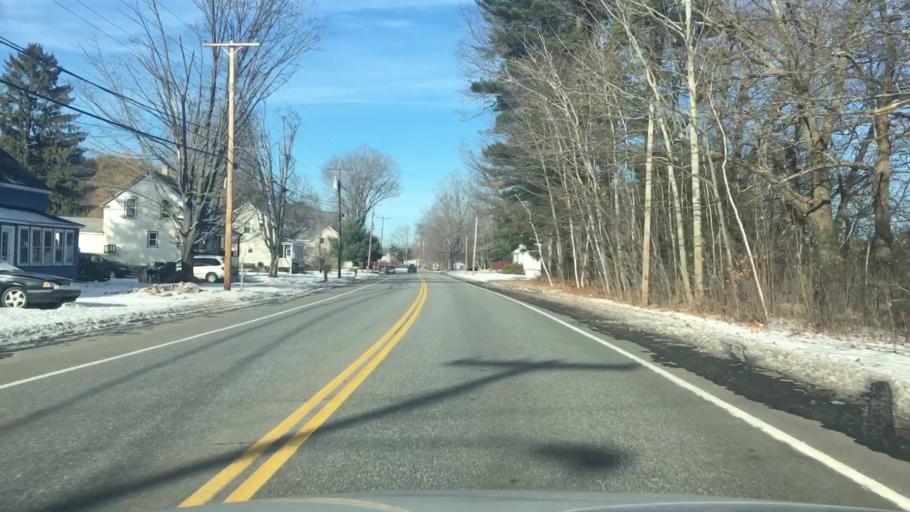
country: US
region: Maine
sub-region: Androscoggin County
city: Lewiston
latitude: 44.0730
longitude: -70.2090
